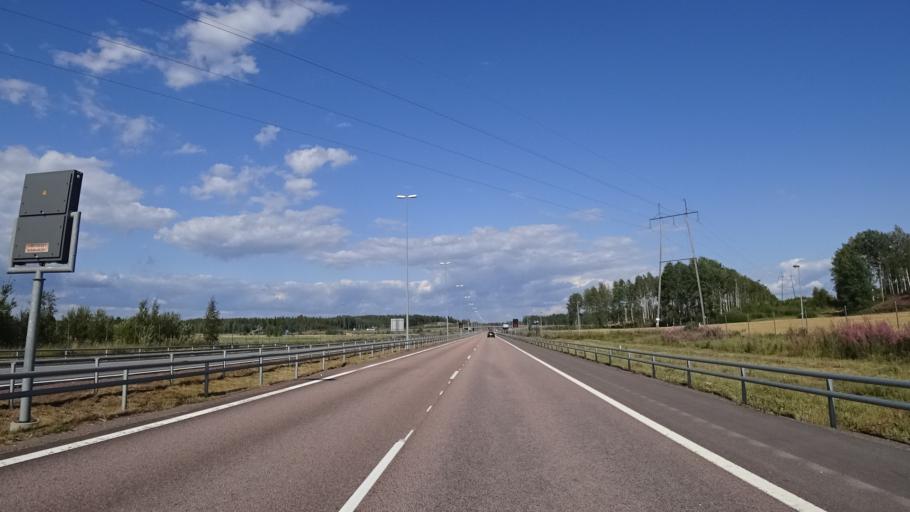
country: FI
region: Kymenlaakso
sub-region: Kotka-Hamina
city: Hamina
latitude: 60.5803
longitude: 27.1437
